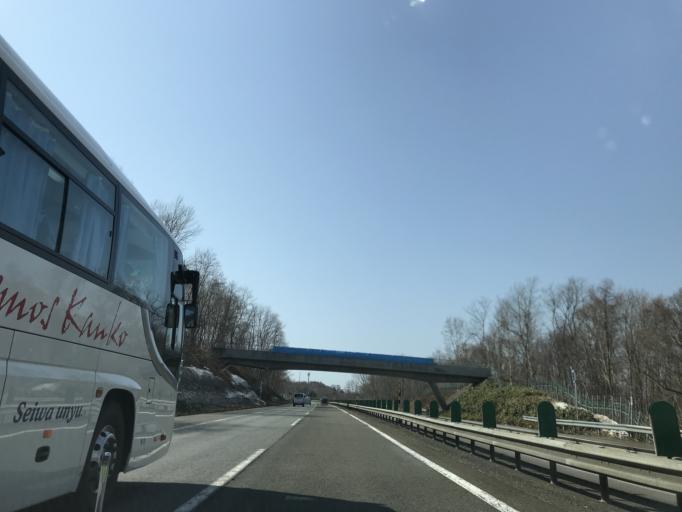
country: JP
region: Hokkaido
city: Bibai
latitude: 43.3189
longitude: 141.8847
